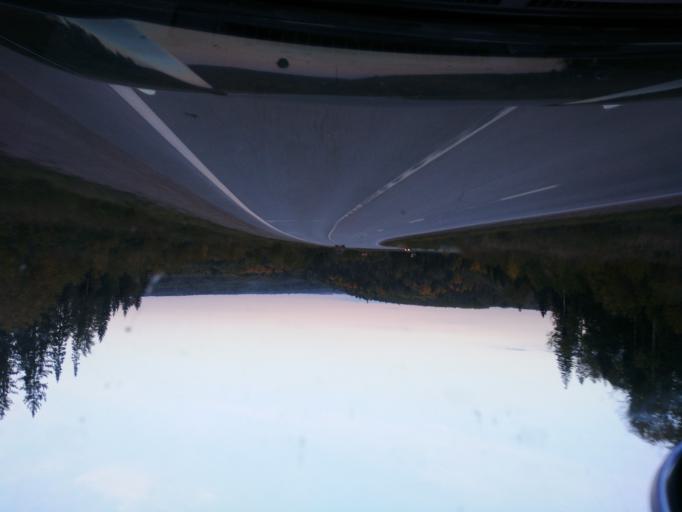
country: RU
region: Perm
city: Polazna
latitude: 58.2887
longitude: 56.5019
